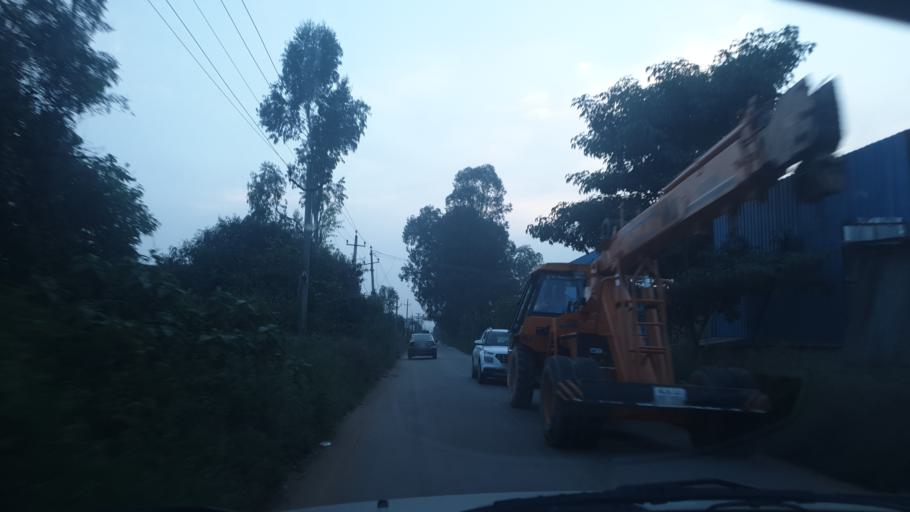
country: IN
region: Karnataka
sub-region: Bangalore Urban
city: Yelahanka
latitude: 13.0601
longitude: 77.6856
